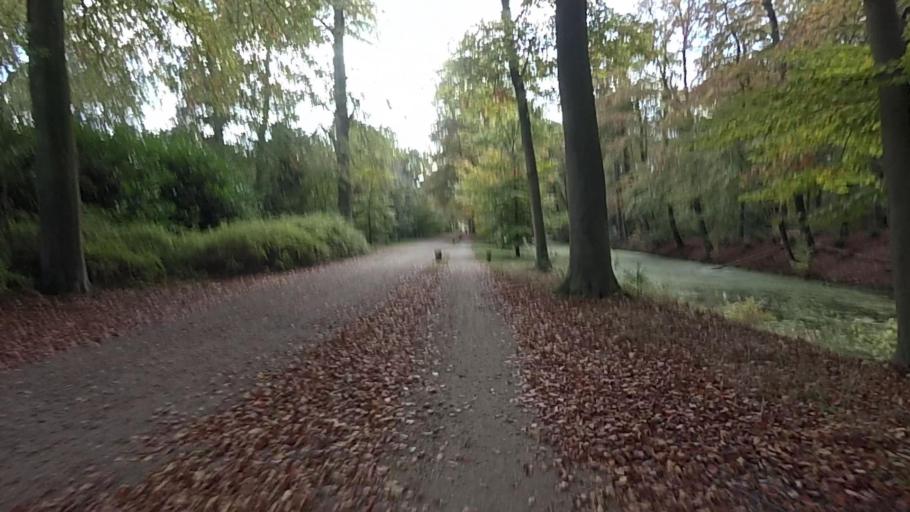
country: NL
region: North Holland
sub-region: Gemeente Wijdemeren
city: Nieuw-Loosdrecht
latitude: 52.2300
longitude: 5.1418
